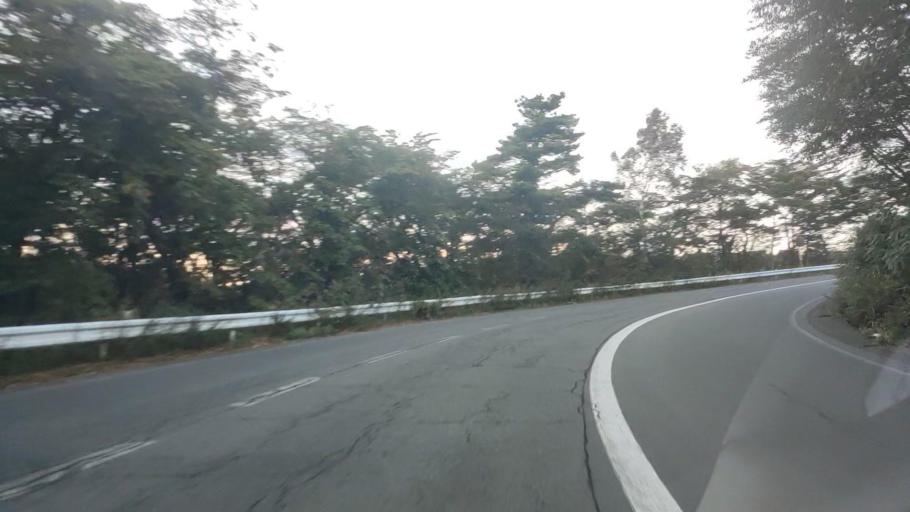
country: JP
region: Nagano
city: Komoro
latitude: 36.3967
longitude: 138.5780
